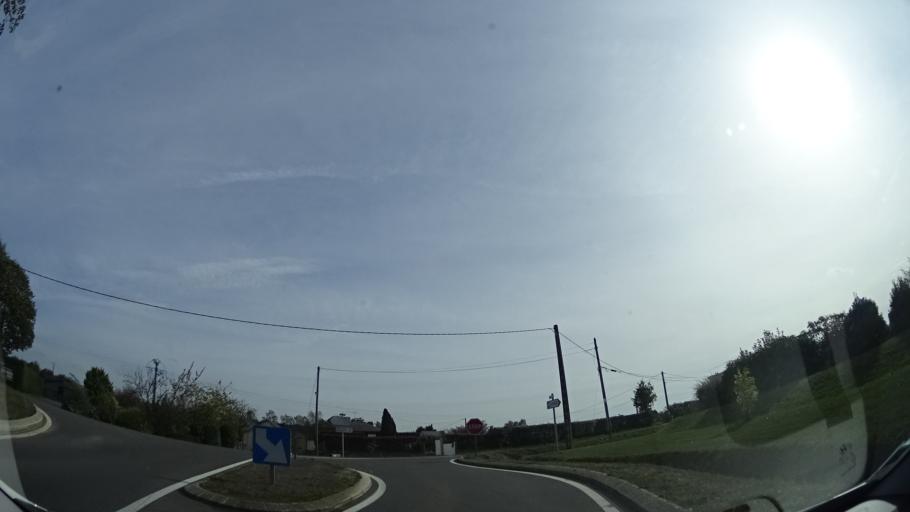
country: FR
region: Brittany
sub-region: Departement d'Ille-et-Vilaine
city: La Meziere
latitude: 48.2235
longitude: -1.7522
